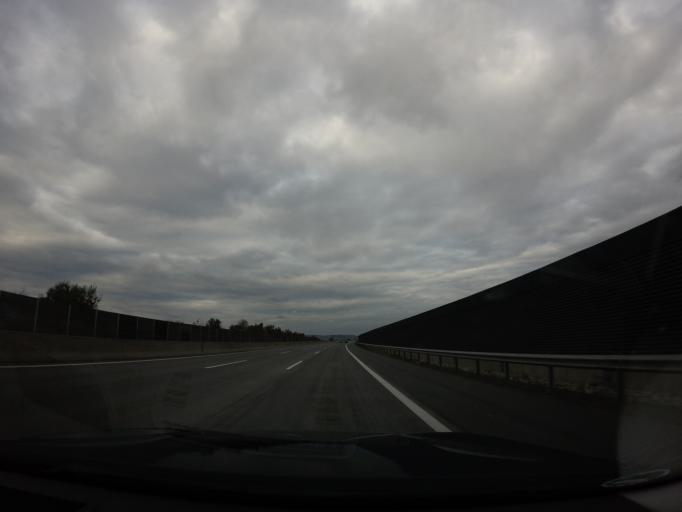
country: AT
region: Lower Austria
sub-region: Politischer Bezirk Melk
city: Pochlarn
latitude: 48.1888
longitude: 15.1959
